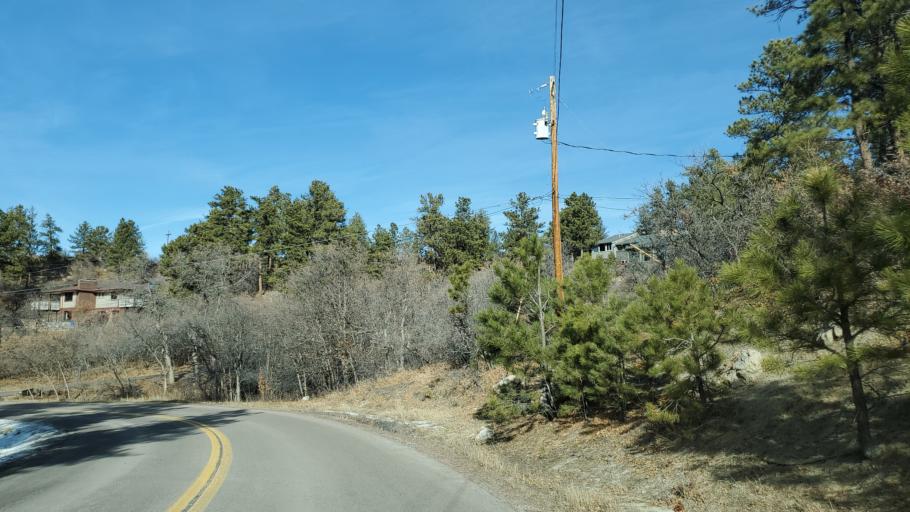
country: US
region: Colorado
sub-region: Douglas County
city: Castle Pines
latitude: 39.4363
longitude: -104.8732
